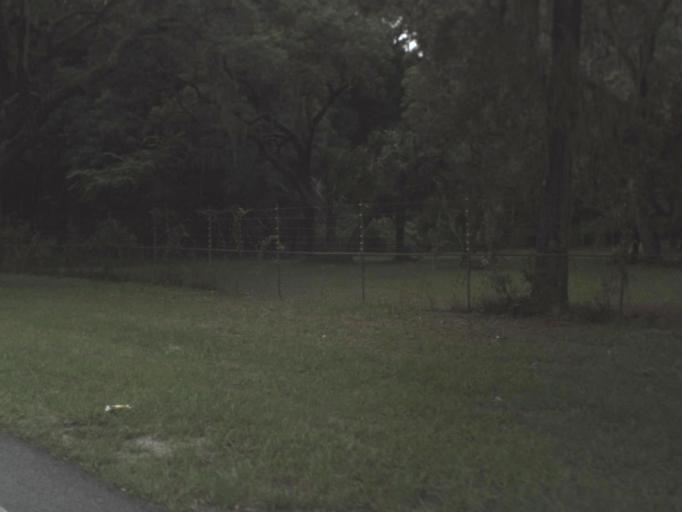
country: US
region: Florida
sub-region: Levy County
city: Chiefland
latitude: 29.4724
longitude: -82.8893
